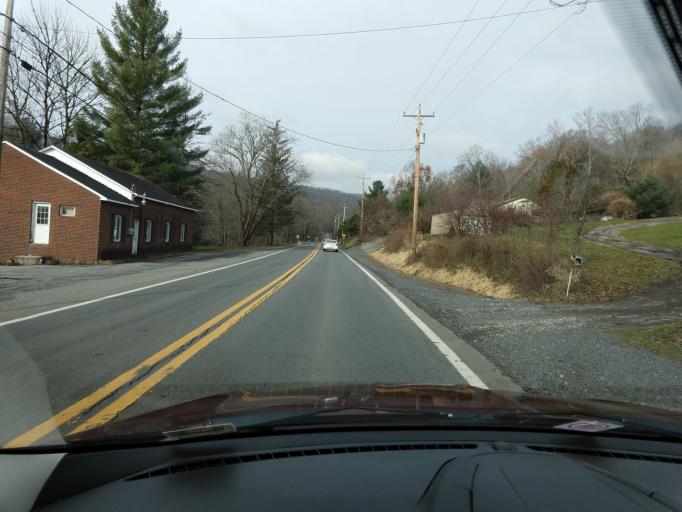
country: US
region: West Virginia
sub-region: Greenbrier County
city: Rainelle
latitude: 37.9854
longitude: -80.7226
